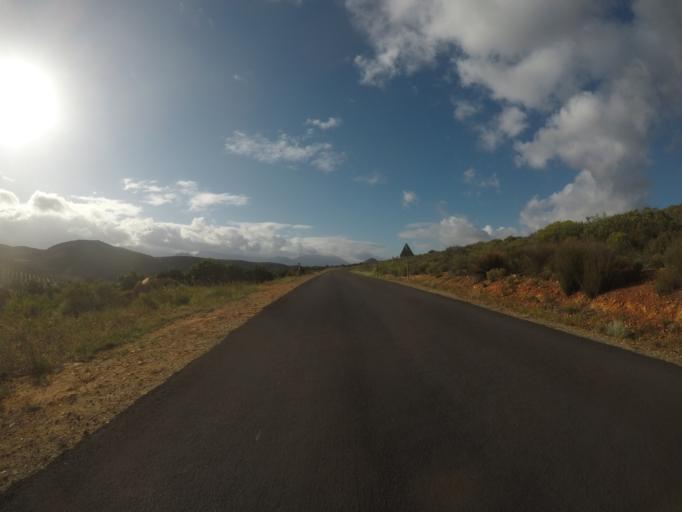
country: ZA
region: Western Cape
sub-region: West Coast District Municipality
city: Clanwilliam
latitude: -32.4219
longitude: 18.9329
